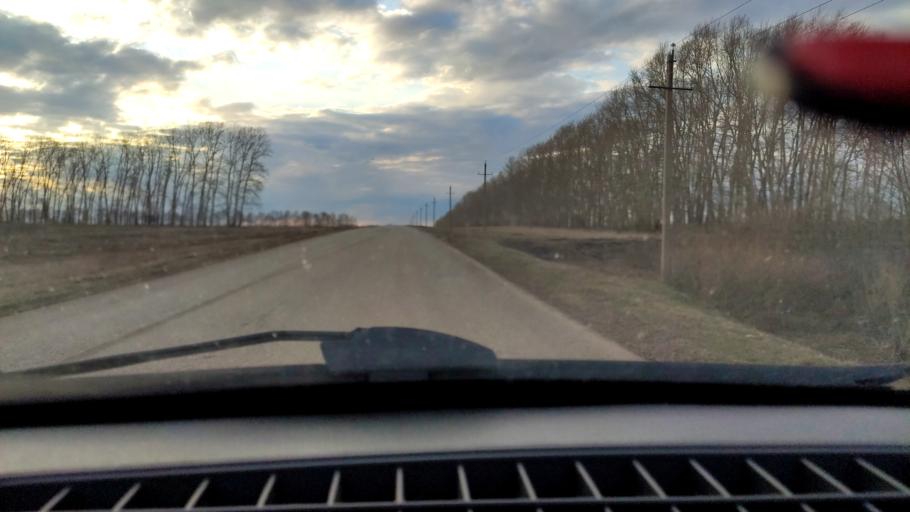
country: RU
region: Bashkortostan
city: Tolbazy
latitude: 53.9936
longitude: 55.7811
